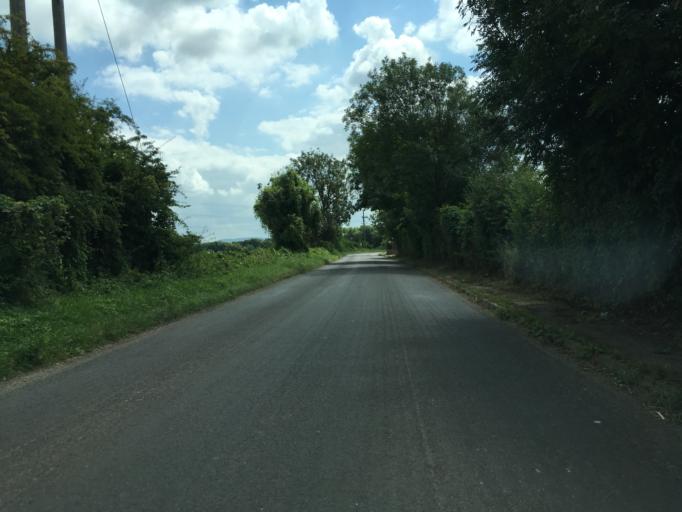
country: GB
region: England
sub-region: Gloucestershire
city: Gloucester
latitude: 51.8860
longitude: -2.2503
